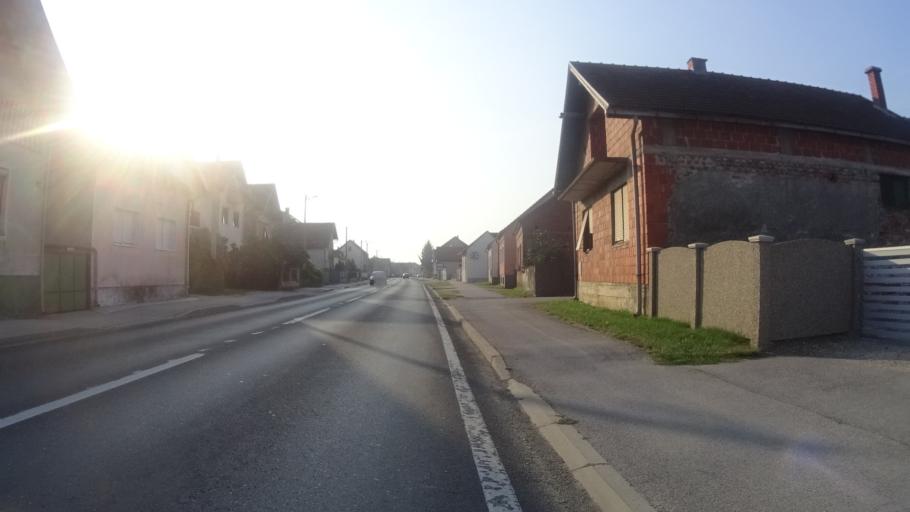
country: HR
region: Varazdinska
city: Petrijanec
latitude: 46.3413
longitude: 16.2438
